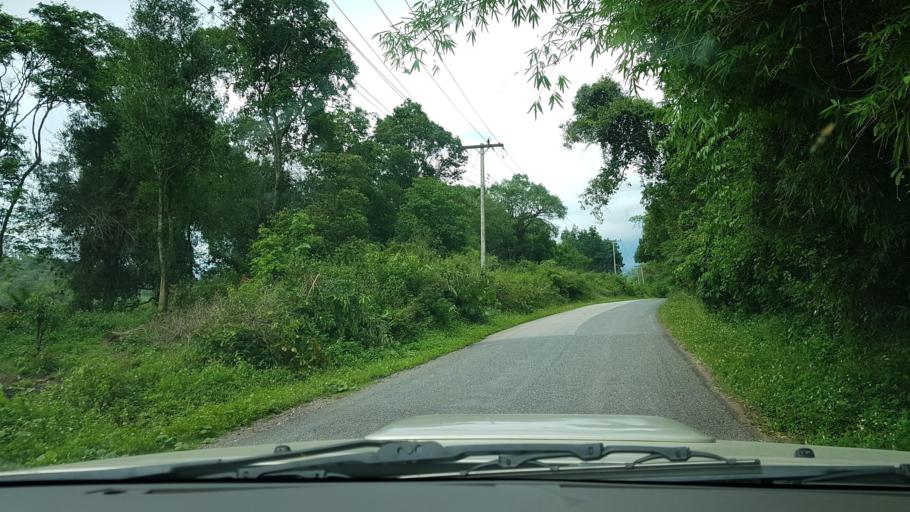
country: LA
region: Loungnamtha
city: Muang Nale
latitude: 20.4057
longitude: 101.7619
